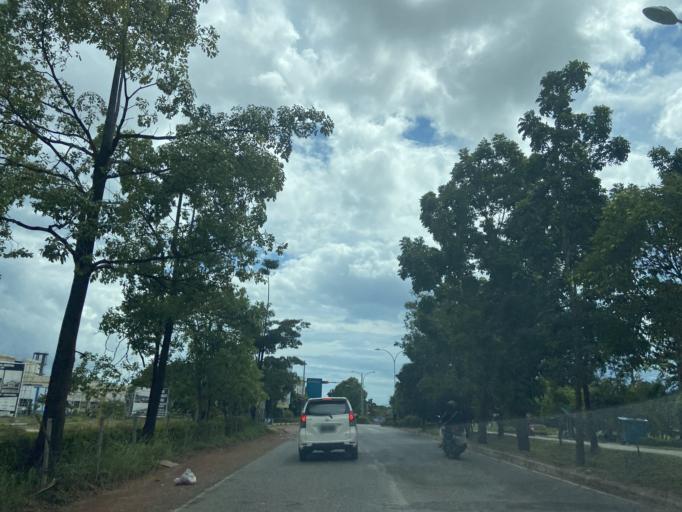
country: SG
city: Singapore
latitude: 1.0442
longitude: 103.9786
